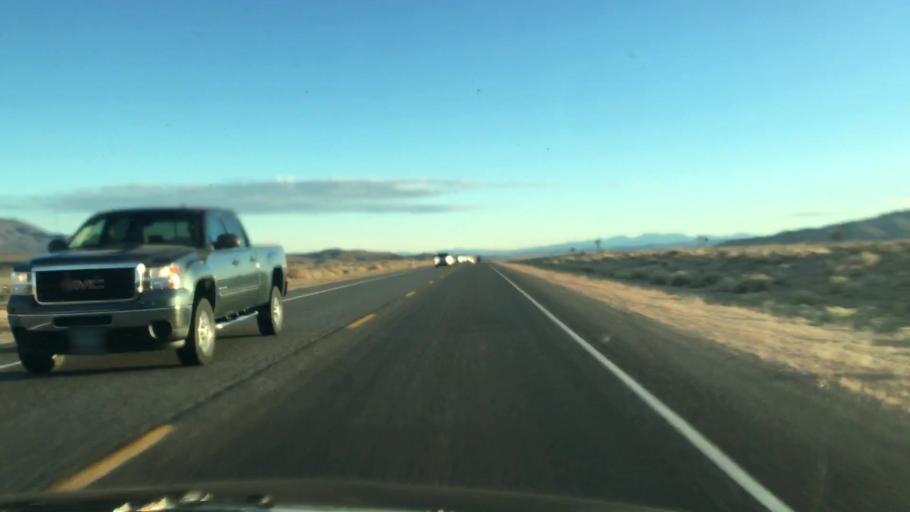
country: US
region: Nevada
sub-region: Esmeralda County
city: Goldfield
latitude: 37.6003
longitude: -117.2123
